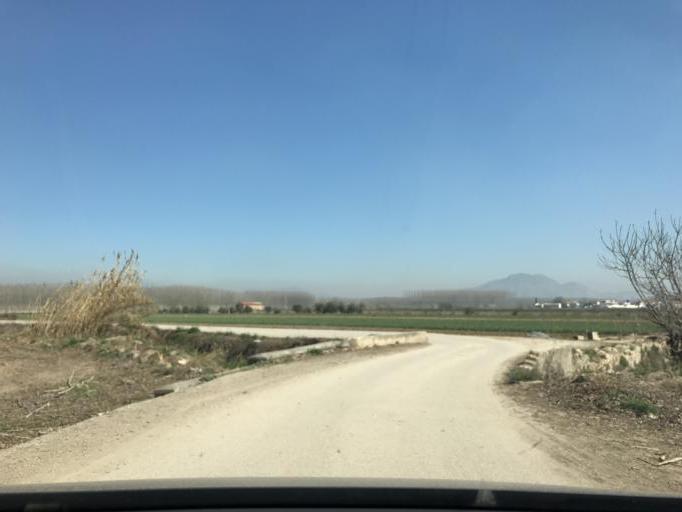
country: ES
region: Andalusia
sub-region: Provincia de Granada
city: Cijuela
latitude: 37.2041
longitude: -3.8106
